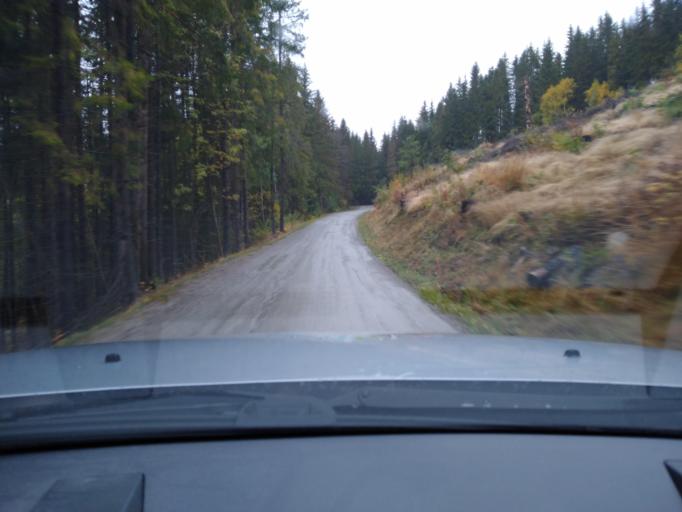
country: NO
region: Oppland
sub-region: Ringebu
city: Ringebu
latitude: 61.5390
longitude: 10.1495
